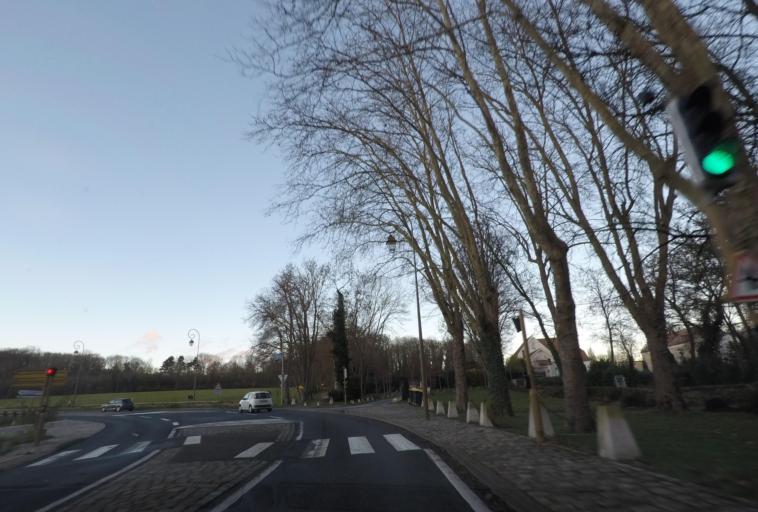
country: FR
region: Ile-de-France
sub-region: Departement de l'Essonne
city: Mennecy
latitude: 48.5782
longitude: 2.4341
